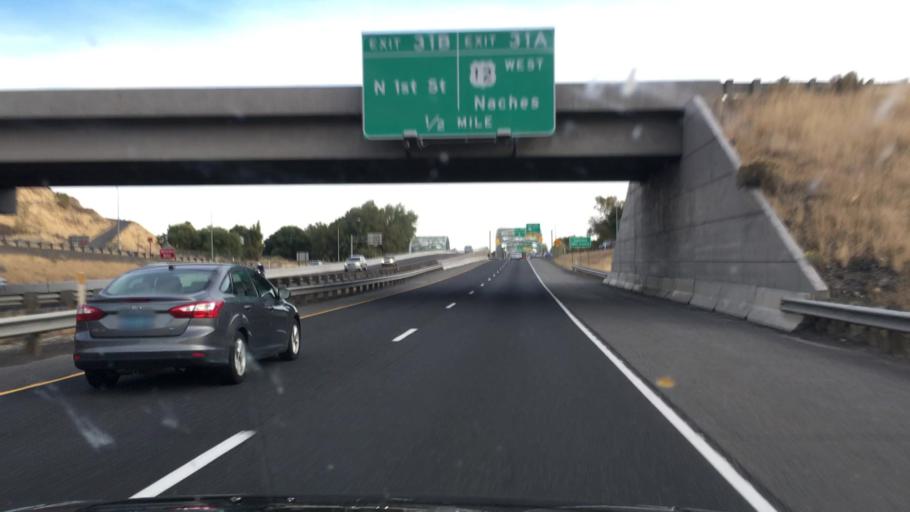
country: US
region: Washington
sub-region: Yakima County
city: Selah
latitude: 46.6331
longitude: -120.5204
